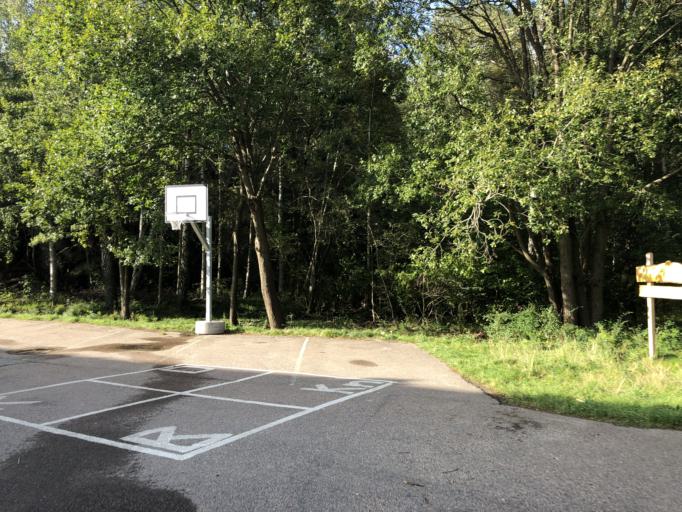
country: SE
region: Vaestra Goetaland
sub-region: Goteborg
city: Majorna
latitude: 57.7328
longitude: 11.9012
